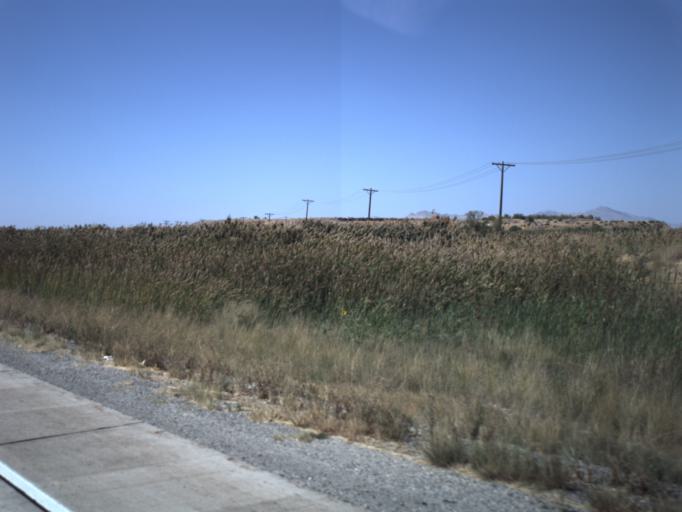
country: US
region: Utah
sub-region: Salt Lake County
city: Magna
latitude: 40.7713
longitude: -112.0578
